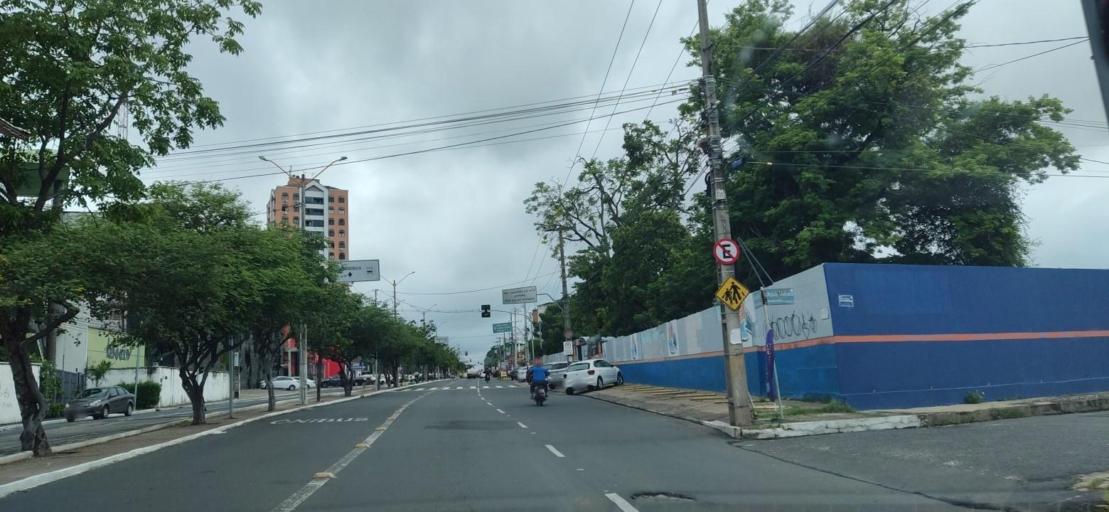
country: BR
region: Piaui
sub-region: Teresina
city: Teresina
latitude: -5.0677
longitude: -42.7708
